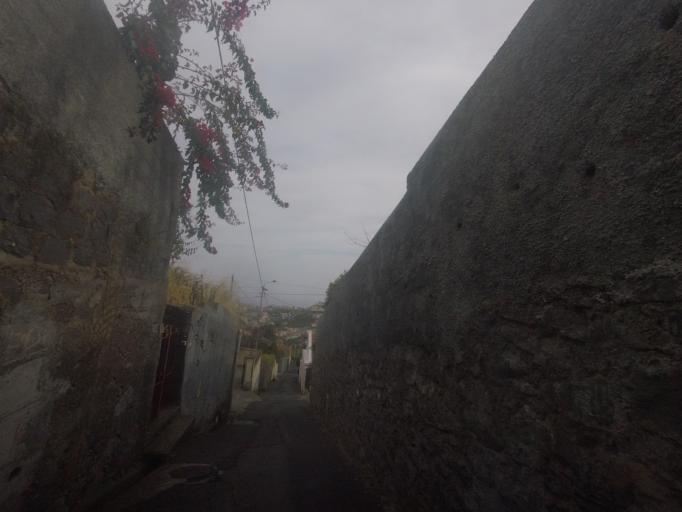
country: PT
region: Madeira
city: Camara de Lobos
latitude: 32.6705
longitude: -16.9476
